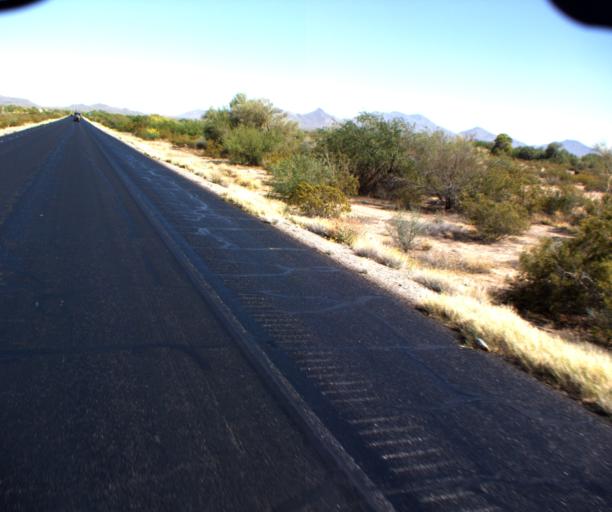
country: US
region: Arizona
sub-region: Pinal County
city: Maricopa
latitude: 32.8435
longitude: -112.2684
